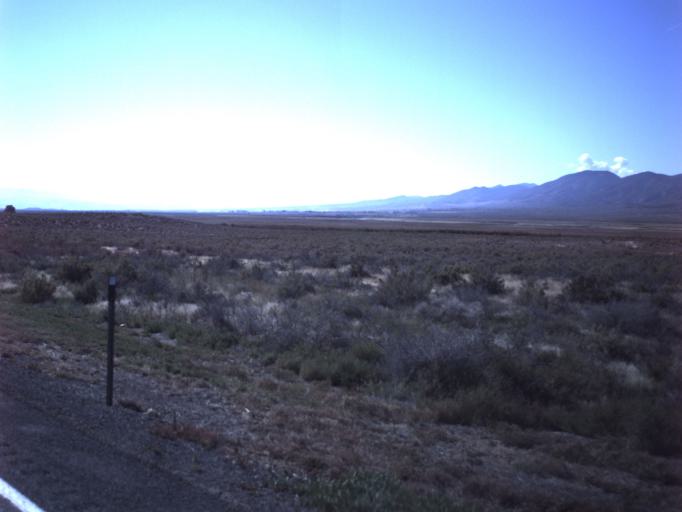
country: US
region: Utah
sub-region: Sanpete County
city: Gunnison
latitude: 39.2941
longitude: -111.8891
